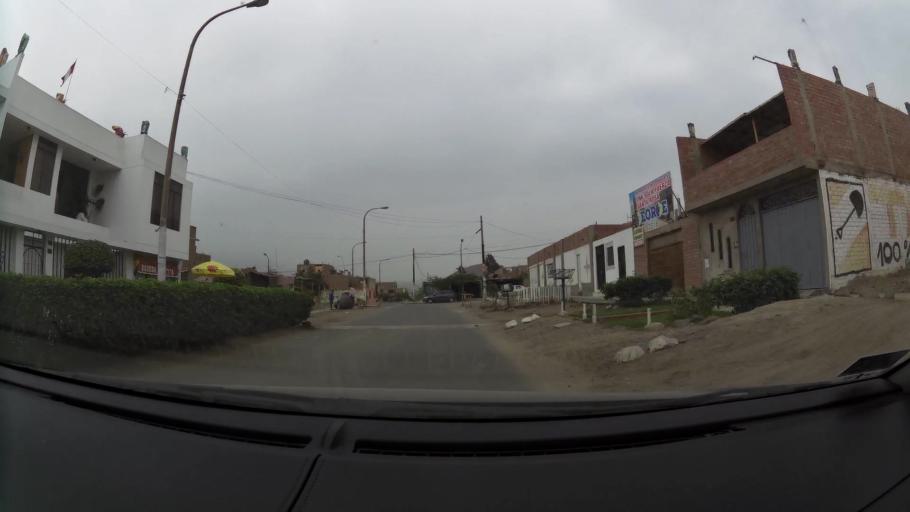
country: PE
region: Lima
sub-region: Lima
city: Santa Rosa
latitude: -11.7894
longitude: -77.1543
